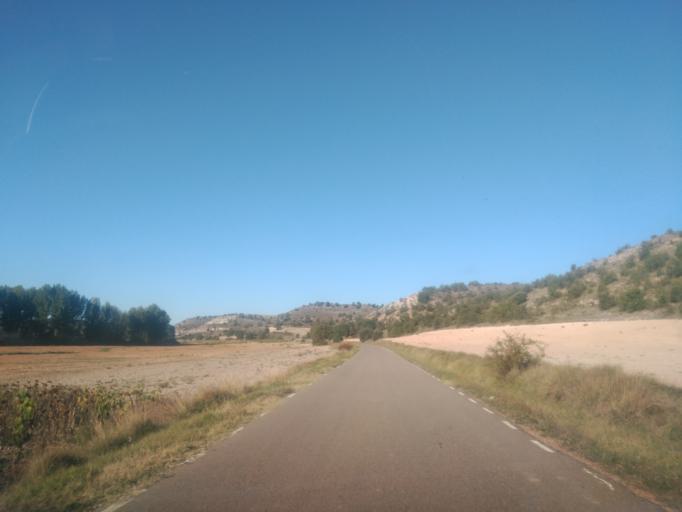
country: ES
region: Castille and Leon
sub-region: Provincia de Burgos
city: Arandilla
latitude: 41.6902
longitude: -3.4146
